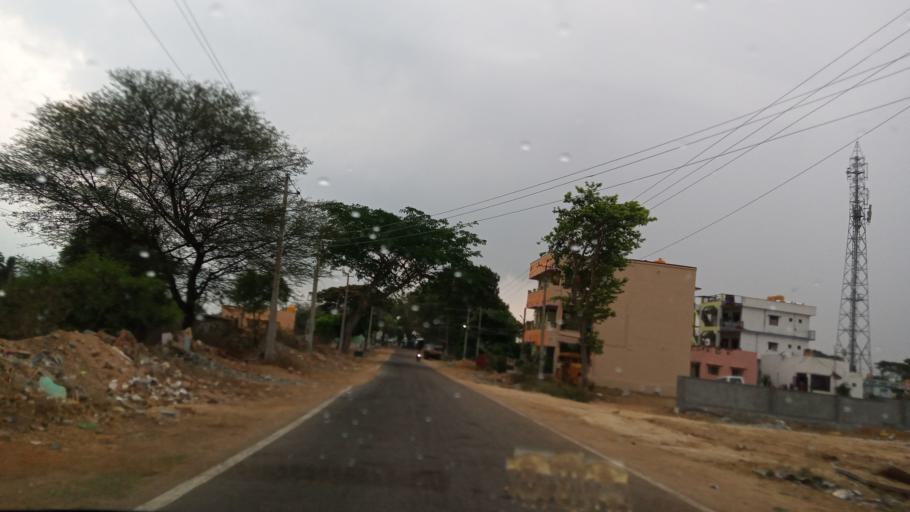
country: IN
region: Karnataka
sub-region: Kolar
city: Mulbagal
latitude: 13.1095
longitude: 78.3353
